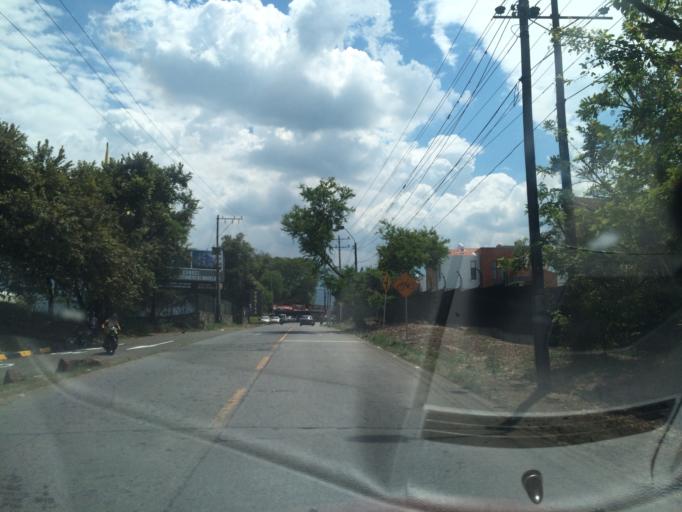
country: CO
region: Valle del Cauca
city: Jamundi
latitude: 3.3423
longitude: -76.5469
